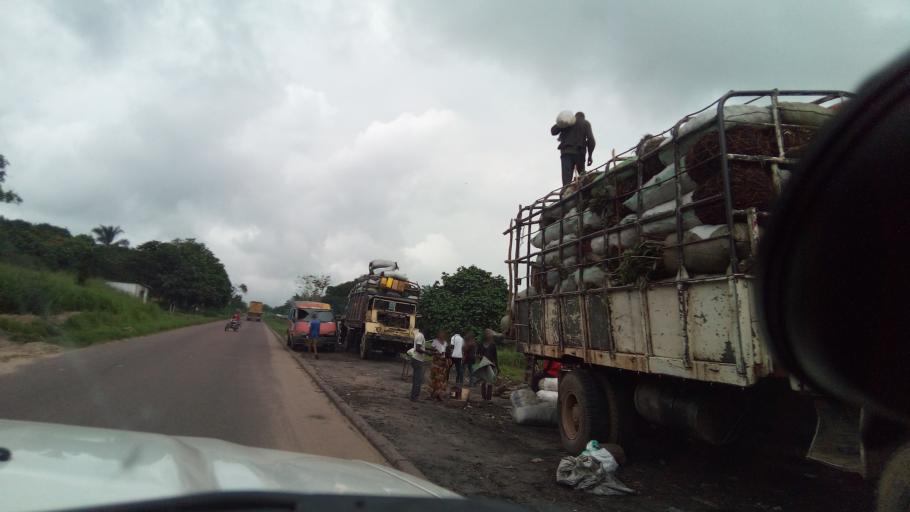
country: CD
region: Bas-Congo
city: Kasangulu
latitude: -4.8306
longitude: 15.1825
